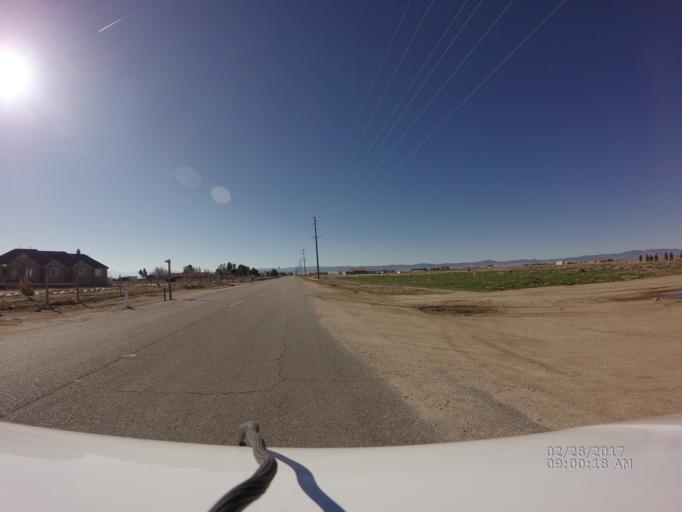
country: US
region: California
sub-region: Kern County
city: Rosamond
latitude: 34.8129
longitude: -118.2552
